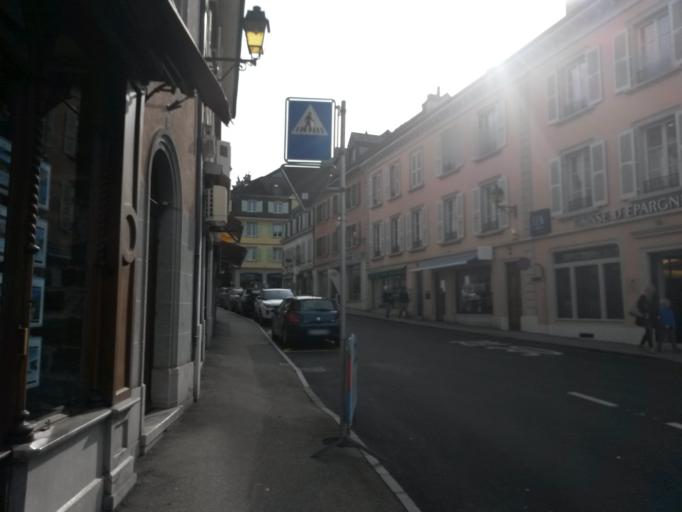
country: CH
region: Vaud
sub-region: Nyon District
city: Nyon
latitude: 46.3832
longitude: 6.2395
